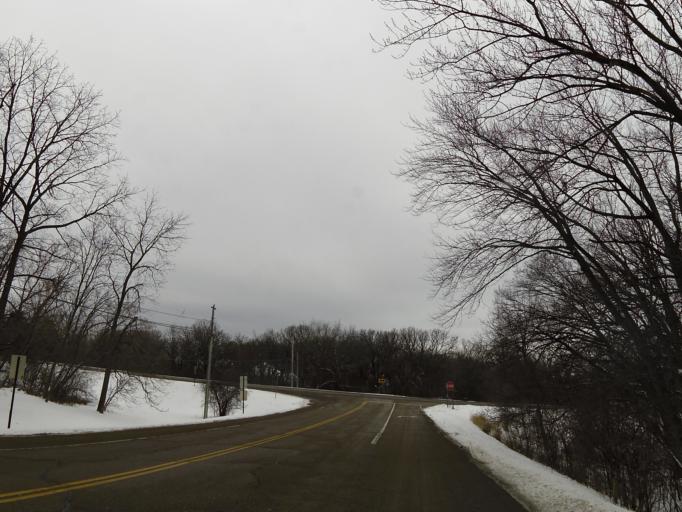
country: US
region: Minnesota
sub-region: Washington County
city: Lakeland
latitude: 44.9641
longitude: -92.8225
